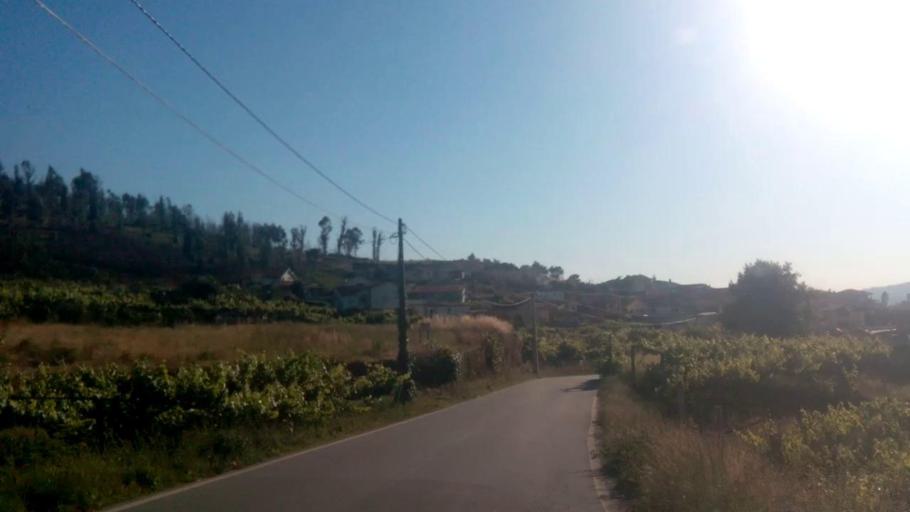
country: PT
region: Porto
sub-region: Penafiel
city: Penafiel
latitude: 41.1978
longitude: -8.2748
